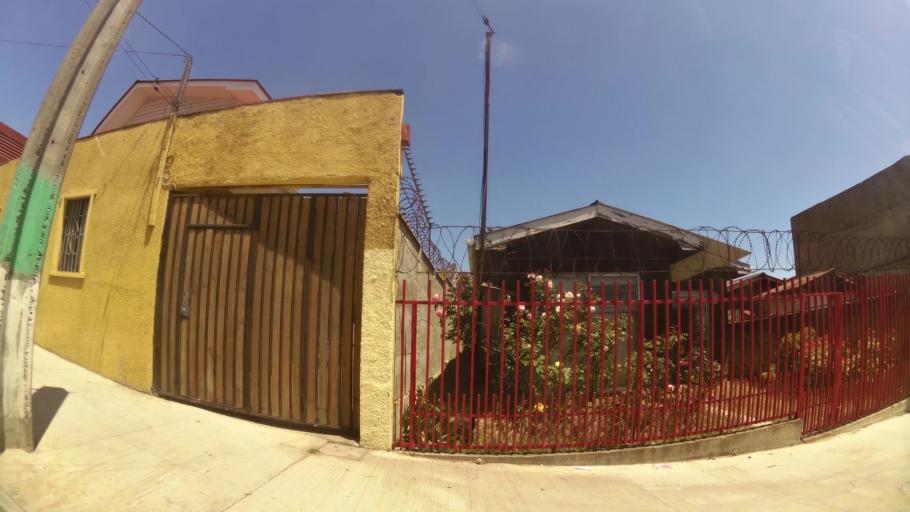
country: CL
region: Valparaiso
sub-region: Provincia de Valparaiso
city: Valparaiso
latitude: -33.0342
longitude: -71.6421
